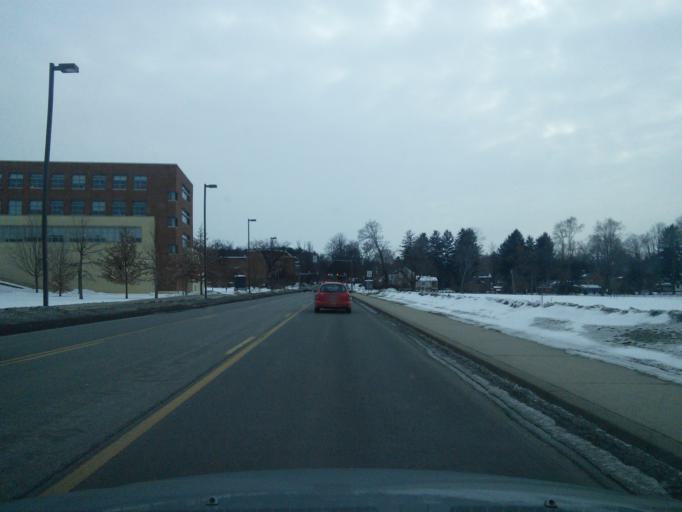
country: US
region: Pennsylvania
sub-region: Centre County
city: State College
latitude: 40.8050
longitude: -77.8654
